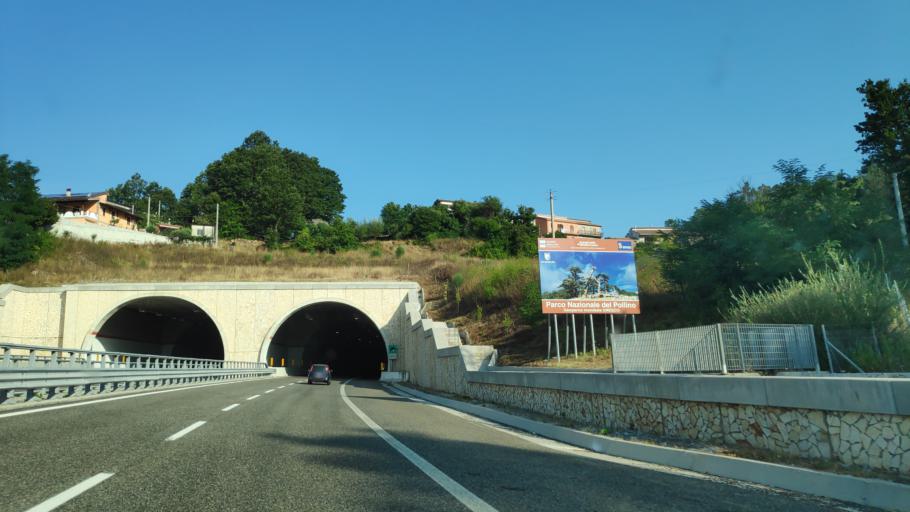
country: IT
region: Basilicate
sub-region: Provincia di Potenza
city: Lauria
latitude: 40.0213
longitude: 15.8809
